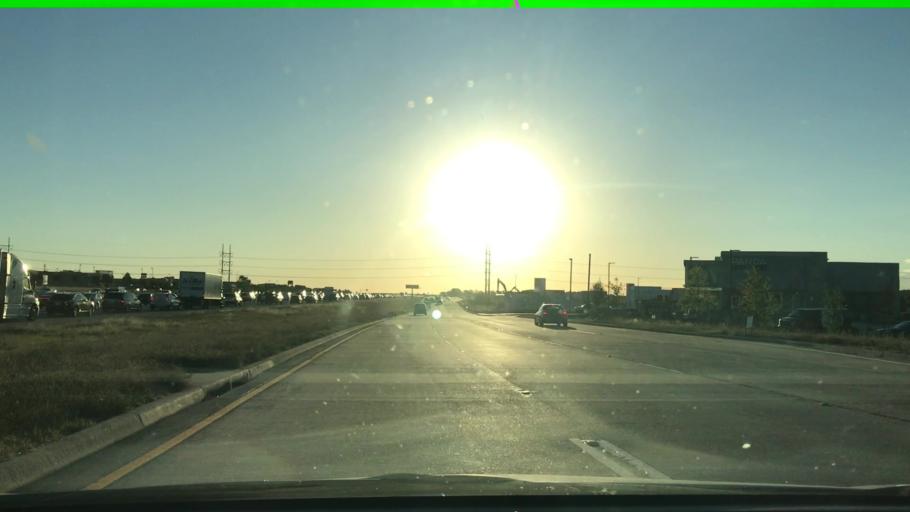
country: US
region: Texas
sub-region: Dallas County
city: Coppell
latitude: 32.9220
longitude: -96.9898
